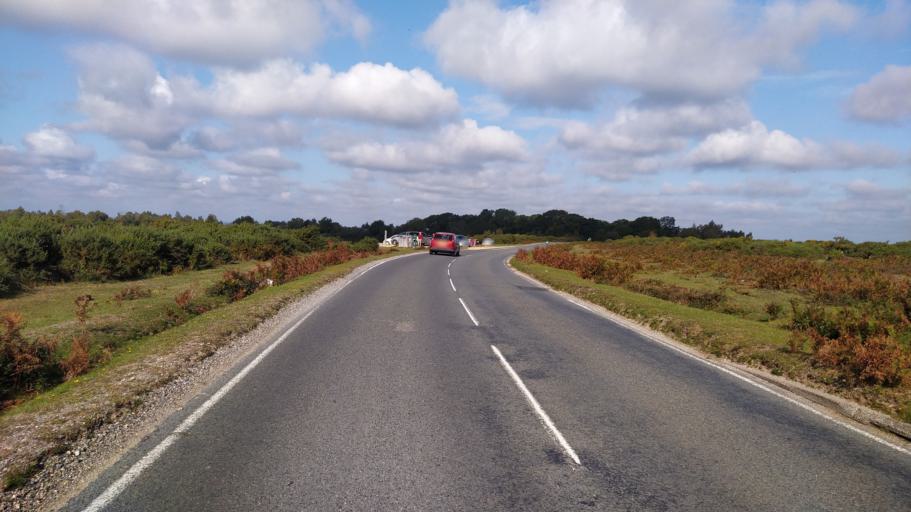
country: GB
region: England
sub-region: Hampshire
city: Ringwood
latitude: 50.8505
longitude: -1.7274
